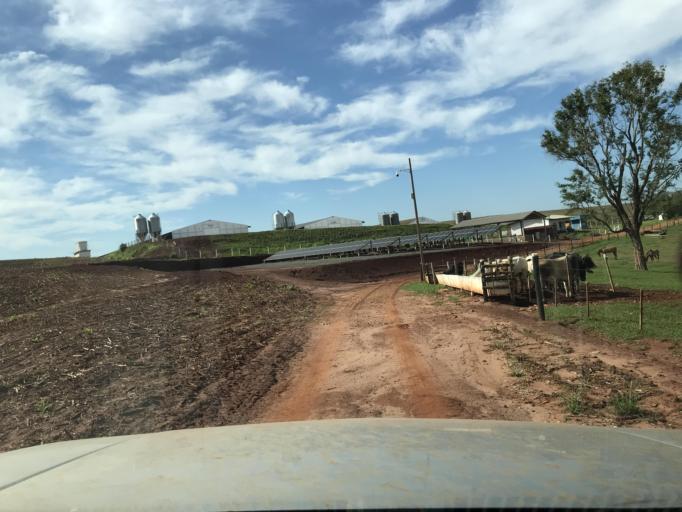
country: BR
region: Parana
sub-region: Palotina
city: Palotina
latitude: -24.1782
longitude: -53.8385
